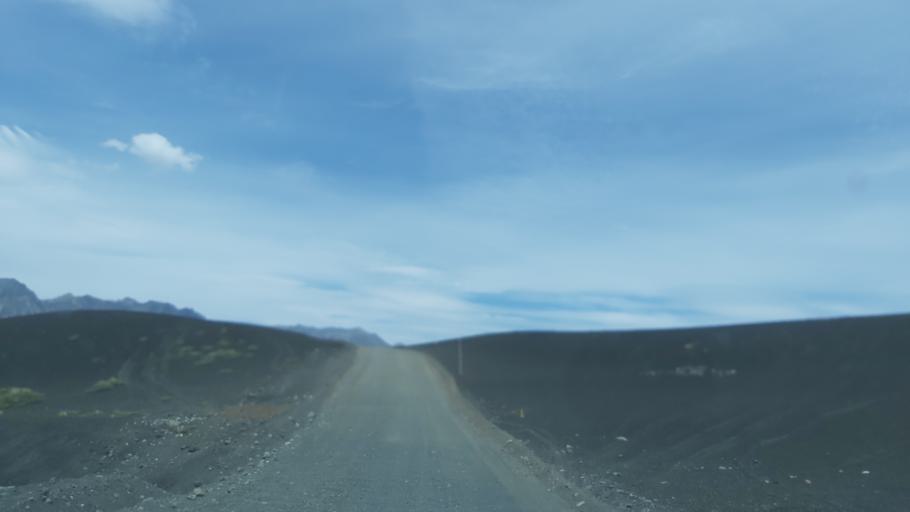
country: AR
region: Neuquen
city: Andacollo
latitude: -37.4131
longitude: -71.2917
